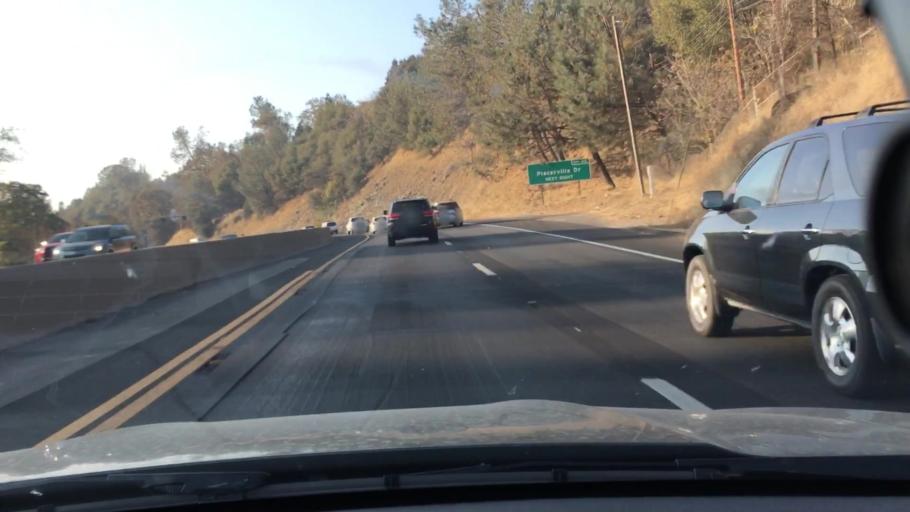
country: US
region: California
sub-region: El Dorado County
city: Placerville
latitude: 38.7289
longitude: -120.8094
